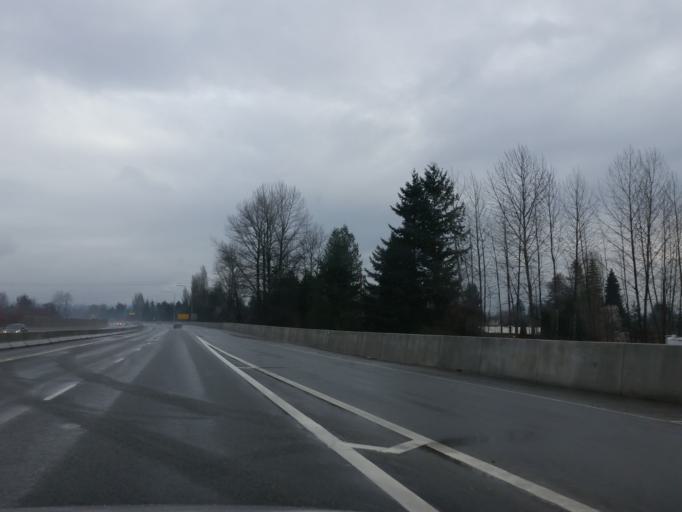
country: US
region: Washington
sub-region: Snohomish County
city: Monroe
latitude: 47.8505
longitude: -122.0032
